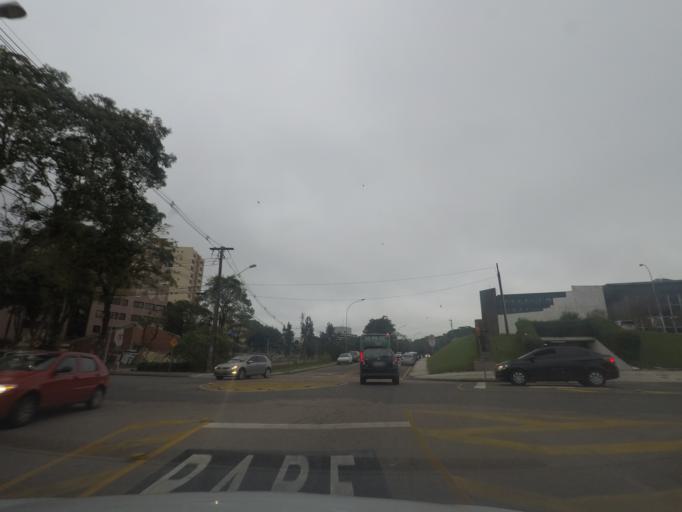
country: BR
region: Parana
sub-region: Curitiba
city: Curitiba
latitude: -25.4136
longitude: -49.2701
